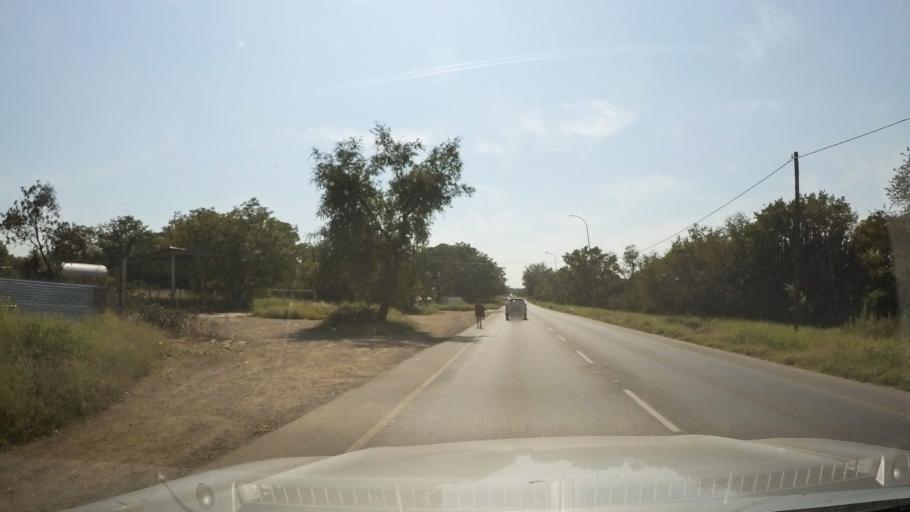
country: BW
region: South East
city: Lobatse
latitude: -25.2245
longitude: 25.6777
